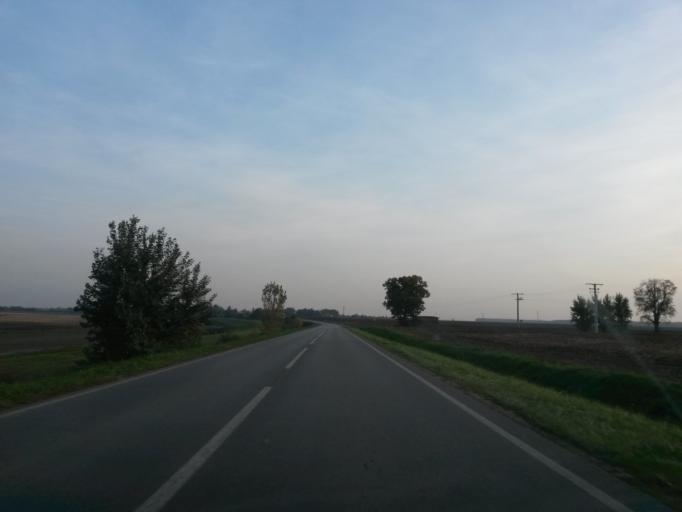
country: HR
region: Osjecko-Baranjska
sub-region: Grad Osijek
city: Karanac
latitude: 45.7122
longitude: 18.7327
